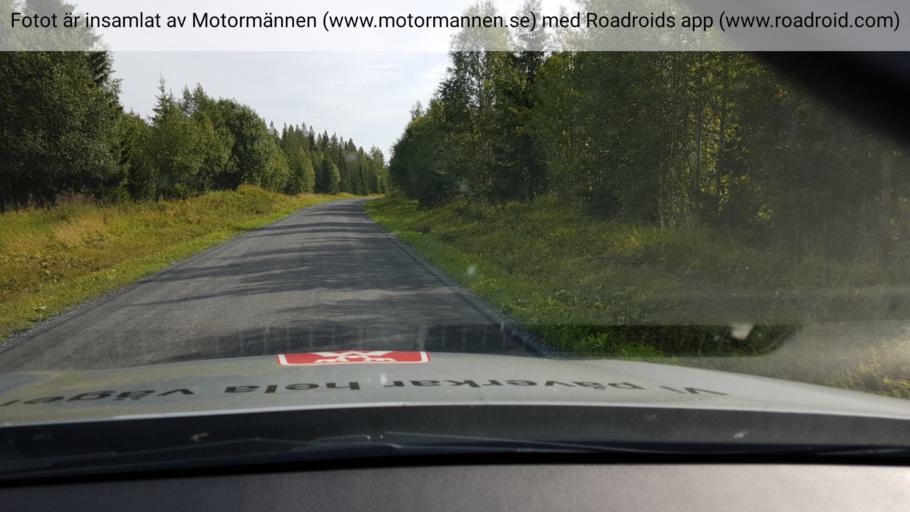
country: SE
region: Jaemtland
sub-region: Krokoms Kommun
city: Valla
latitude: 63.3465
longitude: 13.9994
